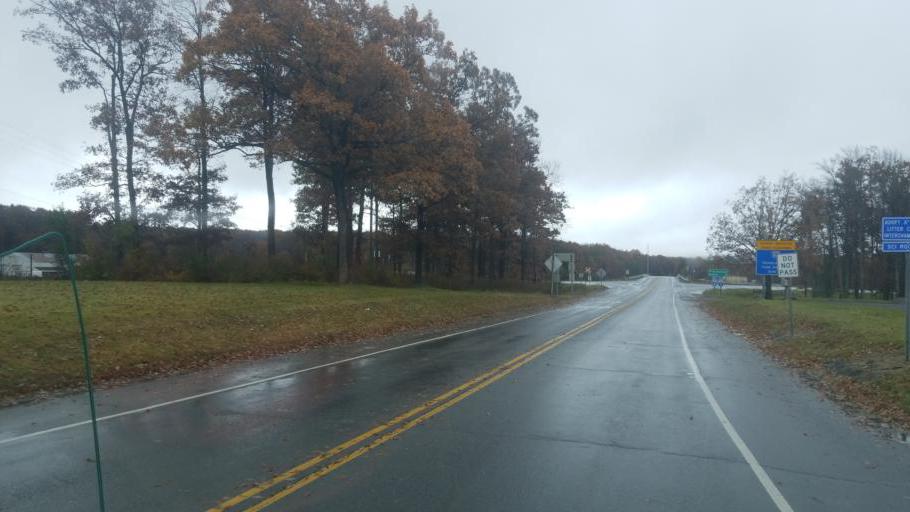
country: US
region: Pennsylvania
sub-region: Centre County
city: Milesburg
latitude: 41.0266
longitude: -77.9353
